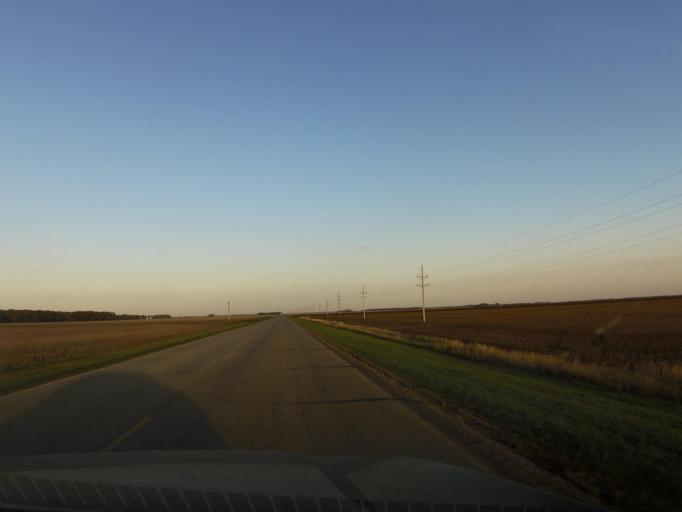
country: CA
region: Manitoba
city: Altona
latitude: 48.9633
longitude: -97.6380
